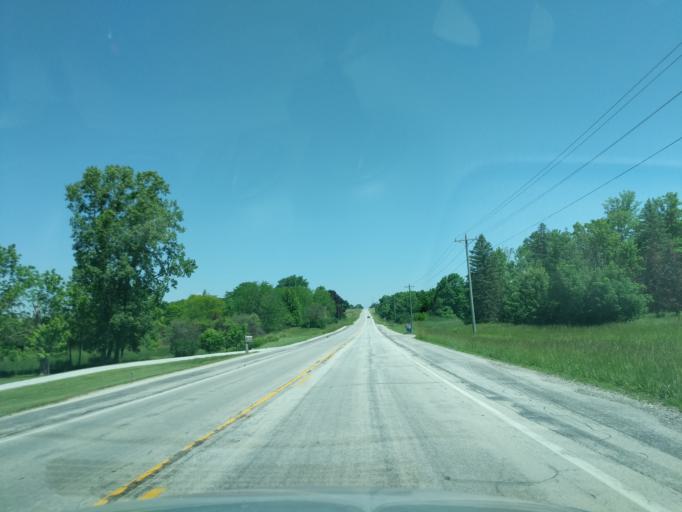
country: US
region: Indiana
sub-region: Whitley County
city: Columbia City
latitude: 41.1993
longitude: -85.4916
